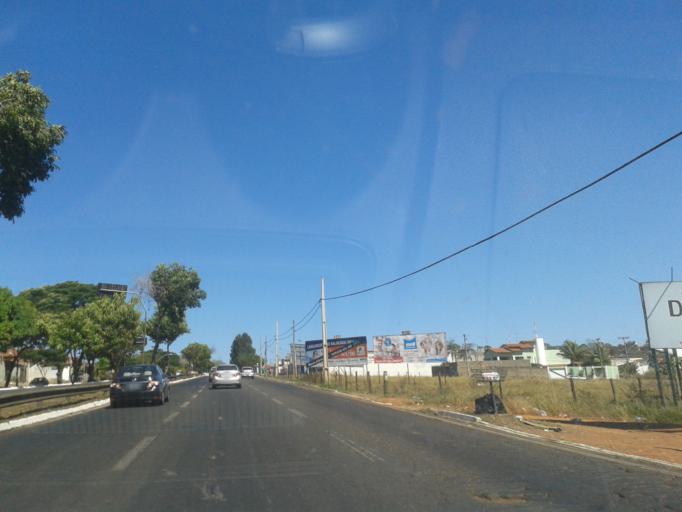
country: BR
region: Goias
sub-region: Goiania
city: Goiania
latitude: -16.6356
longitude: -49.2832
